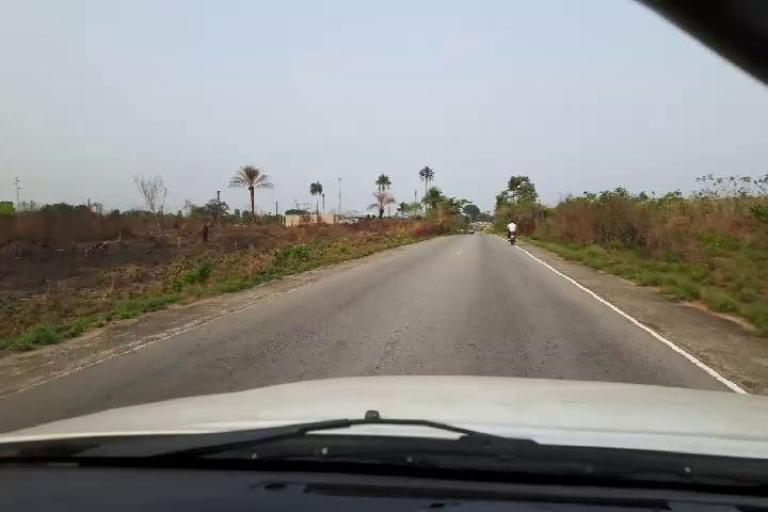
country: SL
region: Southern Province
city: Baoma
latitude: 7.9287
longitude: -11.5805
